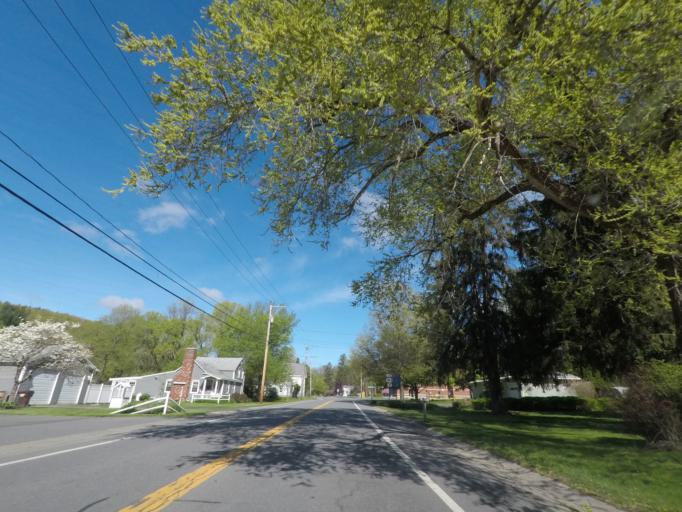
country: US
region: New York
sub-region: Albany County
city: Ravena
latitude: 42.4711
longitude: -73.8940
